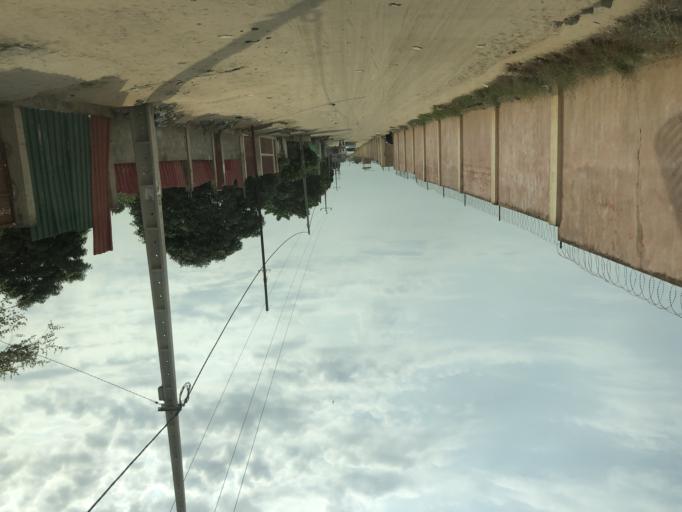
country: AO
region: Luanda
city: Luanda
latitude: -8.8970
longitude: 13.3538
